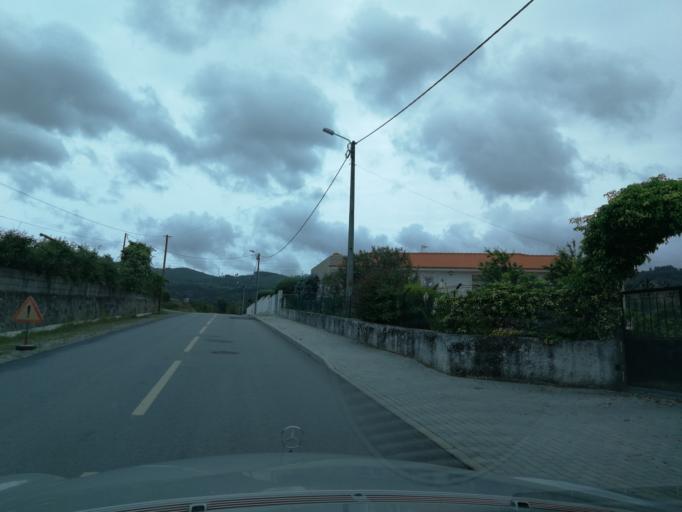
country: PT
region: Braga
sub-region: Braga
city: Adaufe
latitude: 41.5995
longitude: -8.3793
